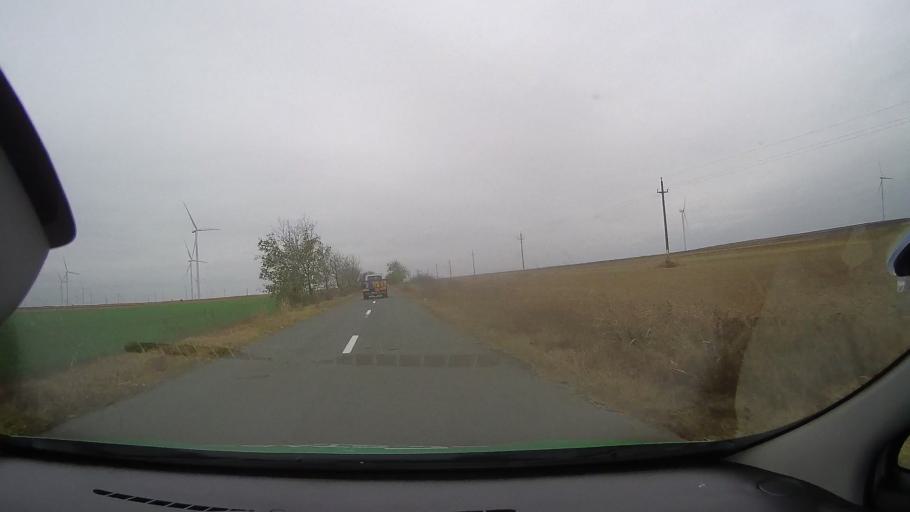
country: RO
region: Constanta
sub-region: Comuna Targusor
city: Targusor
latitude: 44.4766
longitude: 28.3791
